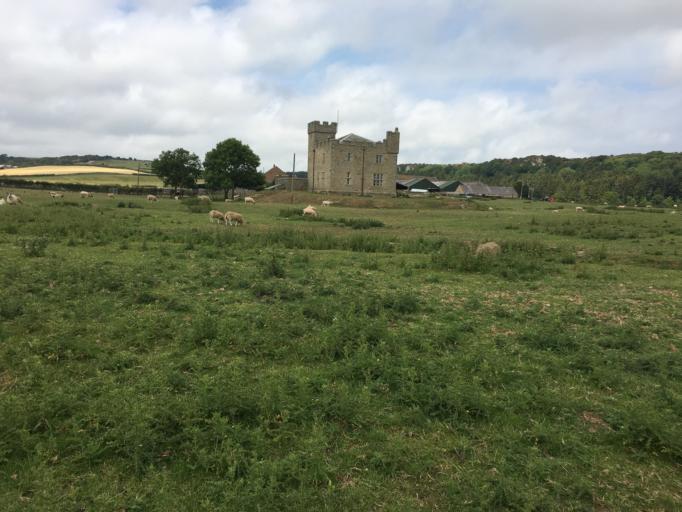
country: GB
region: England
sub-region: Northumberland
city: Belford
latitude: 55.5988
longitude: -1.8366
